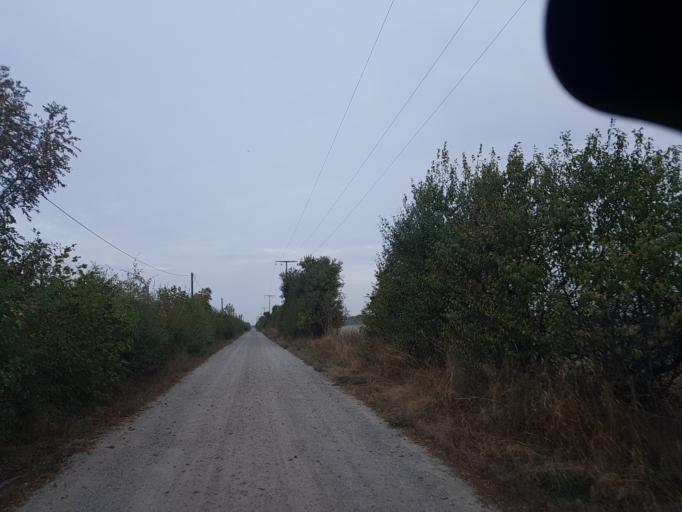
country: DE
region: Saxony-Anhalt
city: Kropstadt
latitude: 52.0032
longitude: 12.8299
